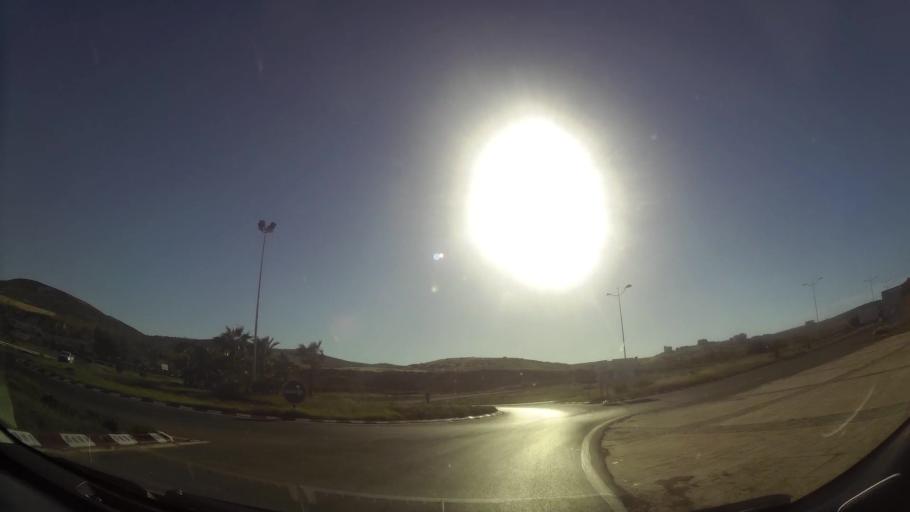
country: MA
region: Oriental
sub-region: Berkane-Taourirt
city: Madagh
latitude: 35.0507
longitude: -2.2184
